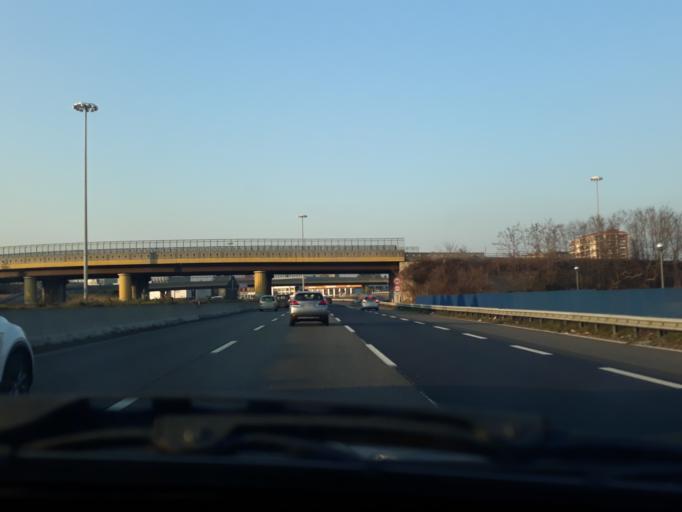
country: IT
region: Lombardy
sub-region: Provincia di Monza e Brianza
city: Muggio
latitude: 45.5951
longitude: 9.2438
